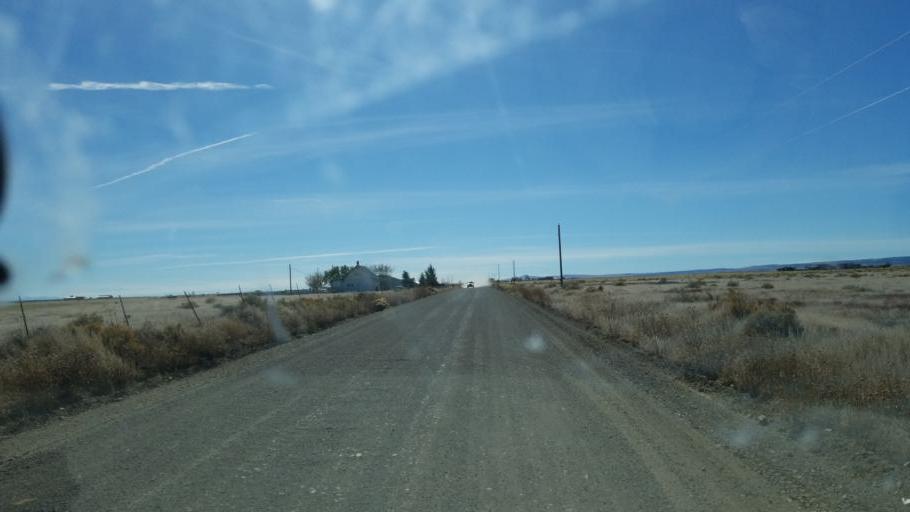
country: US
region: Colorado
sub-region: Rio Grande County
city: Monte Vista
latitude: 37.3890
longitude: -106.1494
